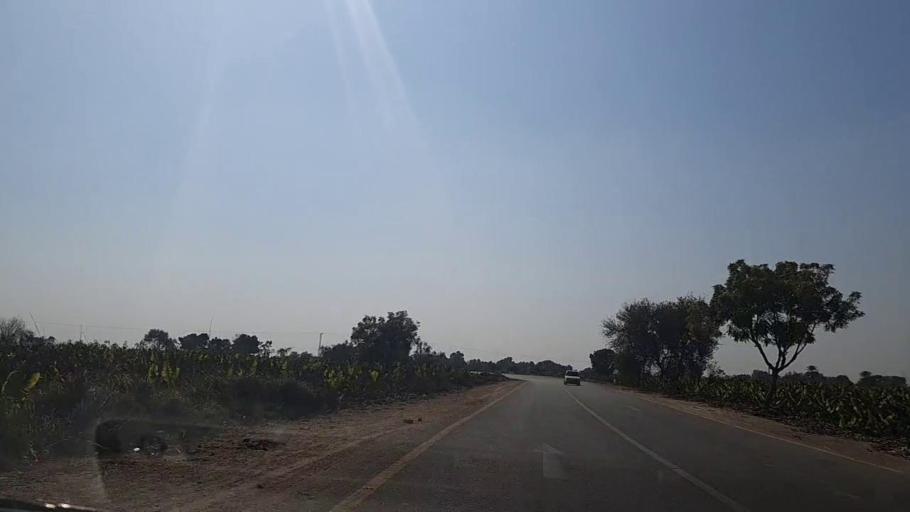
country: PK
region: Sindh
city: Sakrand
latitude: 26.0943
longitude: 68.4024
